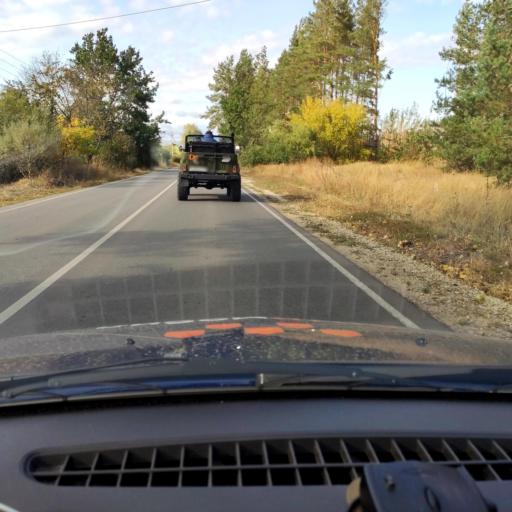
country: RU
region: Voronezj
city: Podgornoye
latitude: 51.8328
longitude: 39.1441
